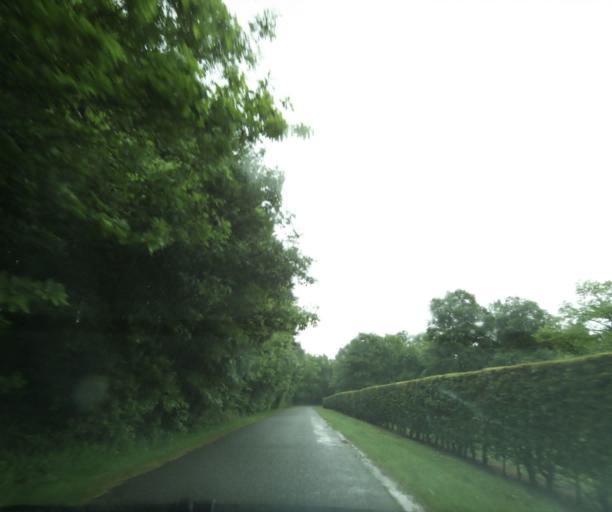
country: FR
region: Bourgogne
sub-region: Departement de Saone-et-Loire
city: Ciry-le-Noble
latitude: 46.5398
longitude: 4.3018
